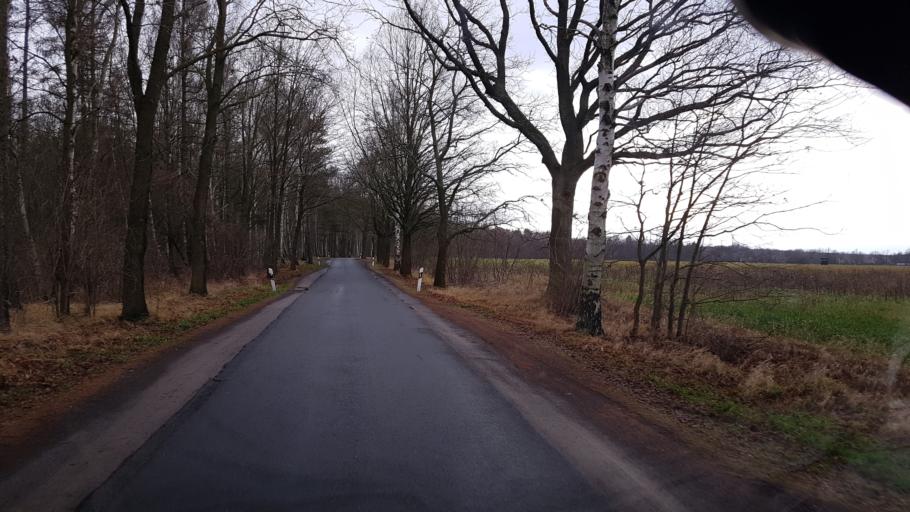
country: DE
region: Brandenburg
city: Altdobern
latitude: 51.6656
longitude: 14.0270
